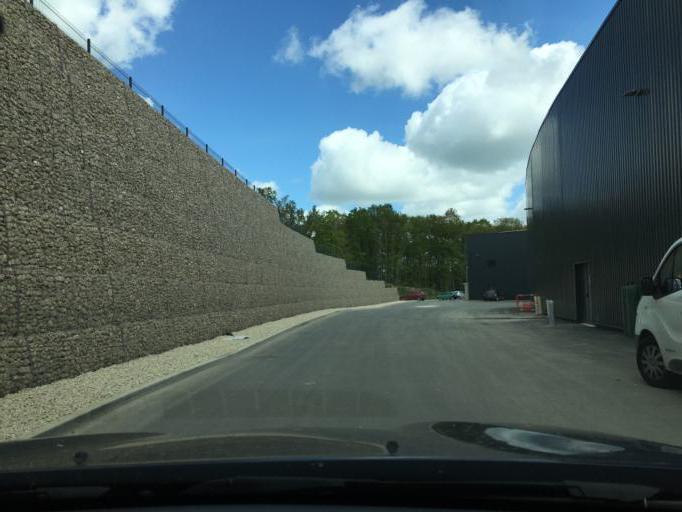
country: FR
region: Centre
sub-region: Departement du Loiret
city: Saran
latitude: 47.9624
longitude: 1.8808
